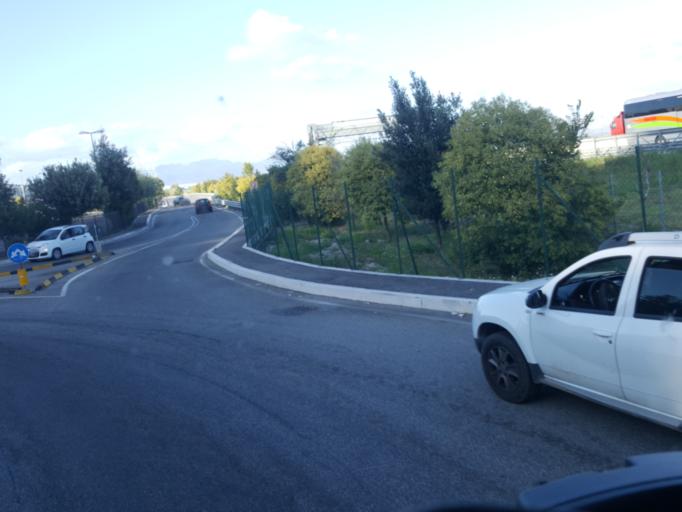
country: IT
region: Latium
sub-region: Citta metropolitana di Roma Capitale
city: Girardi-Bellavista-Terrazze
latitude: 42.1033
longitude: 12.5834
